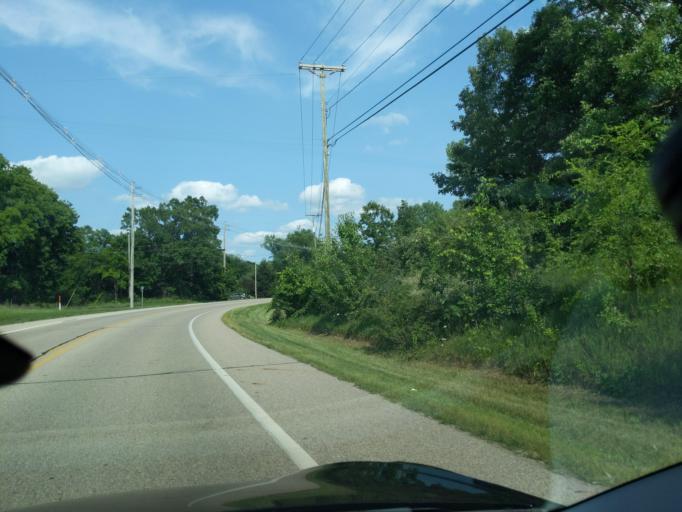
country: US
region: Michigan
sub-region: Kent County
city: Lowell
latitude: 42.9295
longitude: -85.3689
